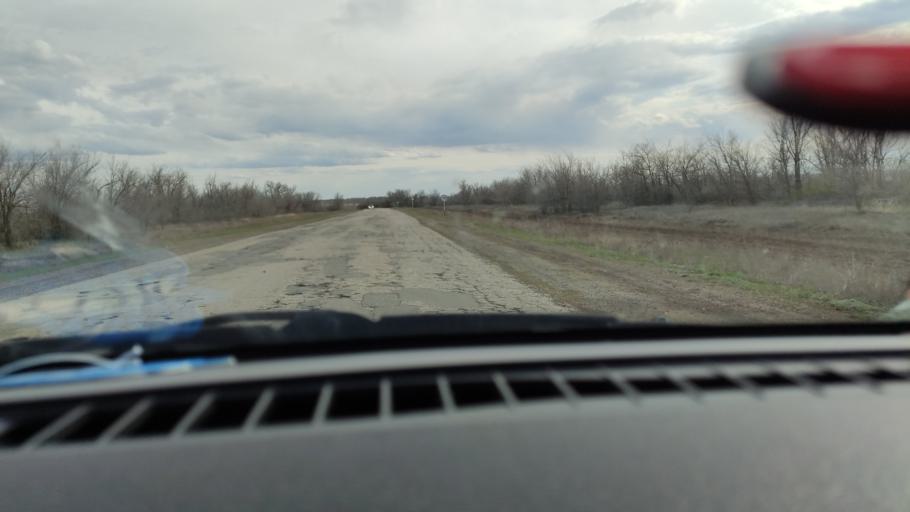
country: RU
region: Saratov
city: Rovnoye
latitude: 50.9621
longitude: 46.1176
